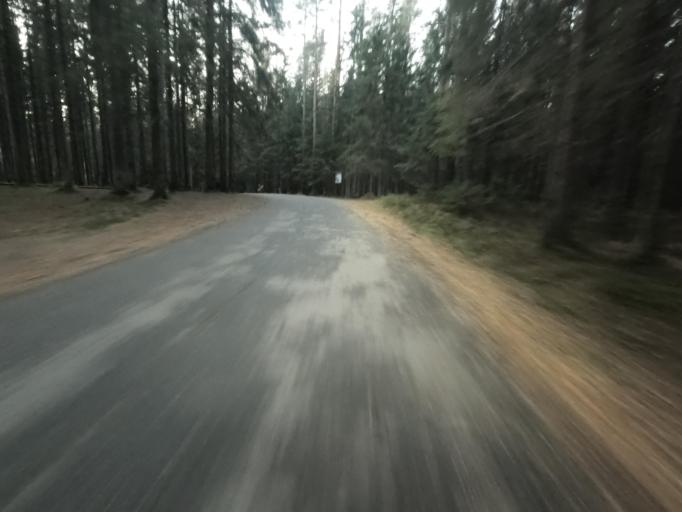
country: RU
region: St.-Petersburg
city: Komarovo
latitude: 60.2073
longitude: 29.7982
